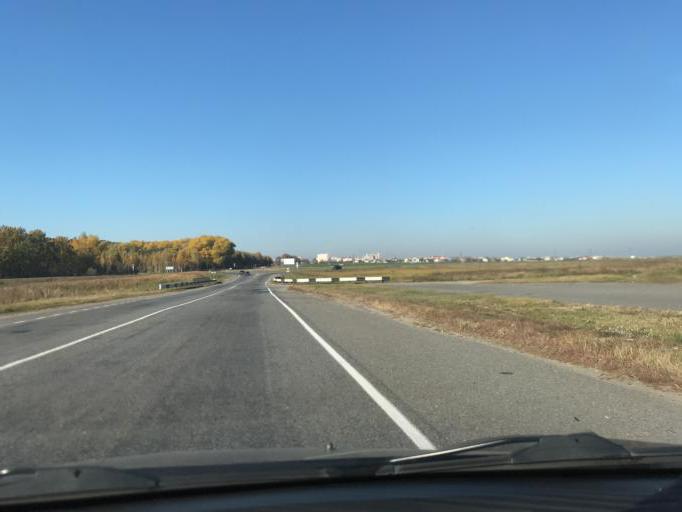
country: BY
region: Gomel
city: Kastsyukowka
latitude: 52.4506
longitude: 30.8281
